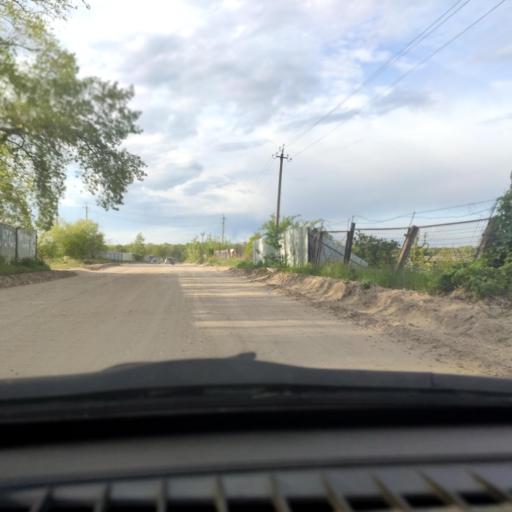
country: RU
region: Samara
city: Zhigulevsk
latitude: 53.4520
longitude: 49.5347
